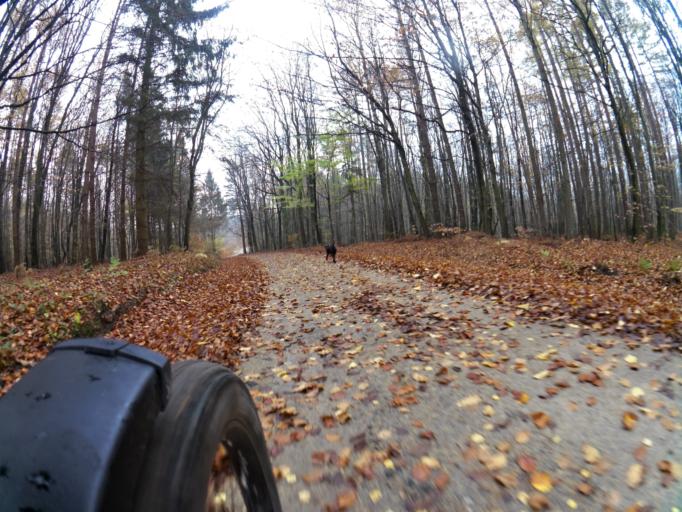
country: PL
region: Pomeranian Voivodeship
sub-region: Powiat pucki
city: Krokowa
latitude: 54.7695
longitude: 18.0934
